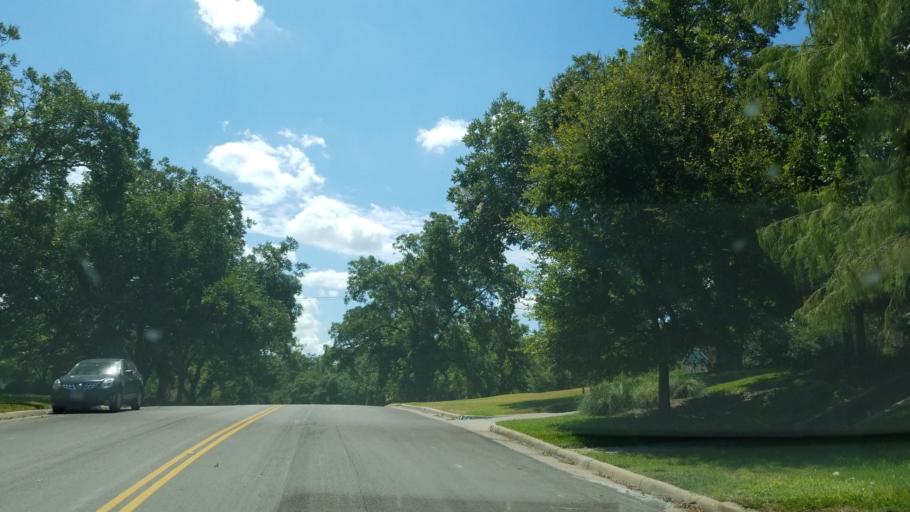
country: US
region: Texas
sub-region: Dallas County
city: Dallas
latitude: 32.7649
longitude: -96.8300
